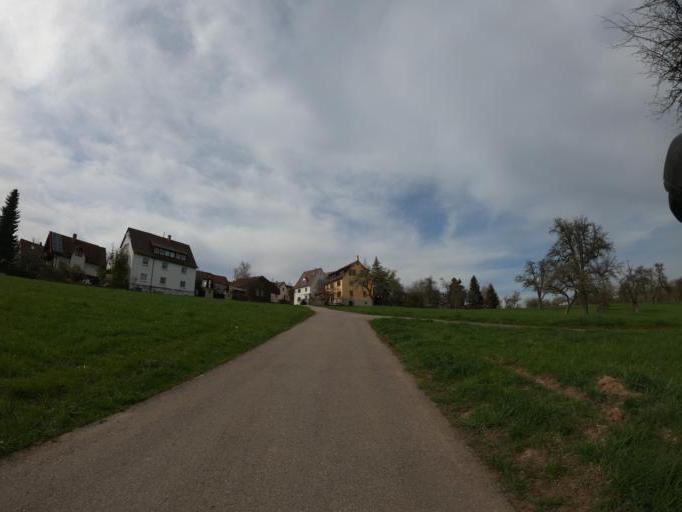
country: DE
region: Baden-Wuerttemberg
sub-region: Regierungsbezirk Stuttgart
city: Ostfildern
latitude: 48.7180
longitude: 9.2364
